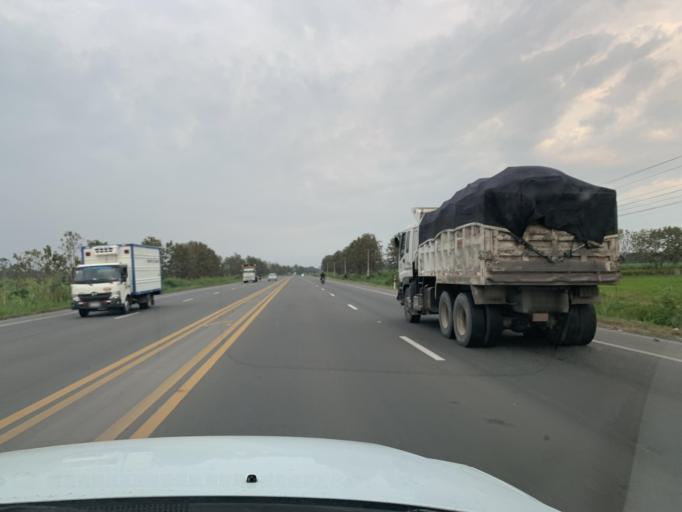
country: EC
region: Guayas
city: Coronel Marcelino Mariduena
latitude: -2.3015
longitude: -79.4890
